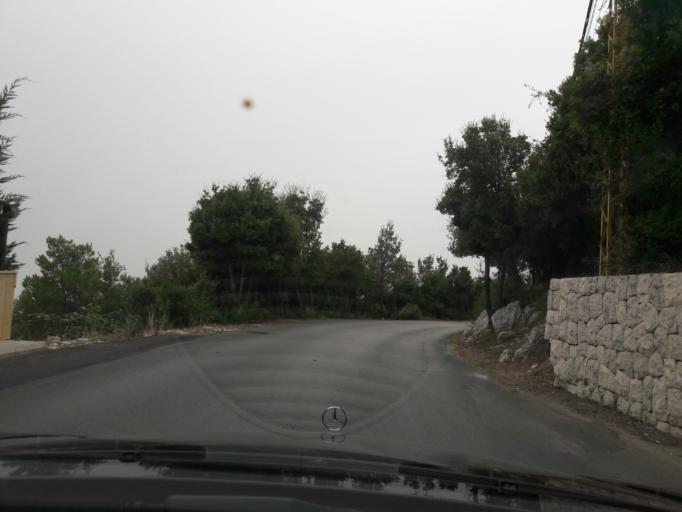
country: LB
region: Mont-Liban
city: Djounie
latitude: 33.9876
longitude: 35.6797
